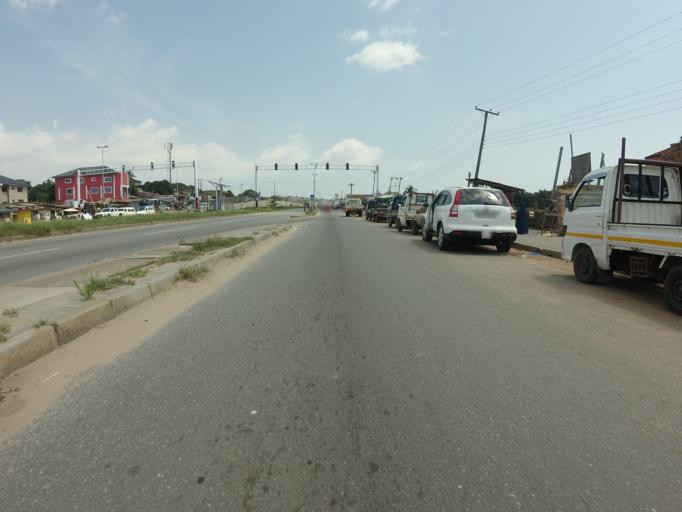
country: GH
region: Greater Accra
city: Gbawe
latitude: 5.6260
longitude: -0.3076
